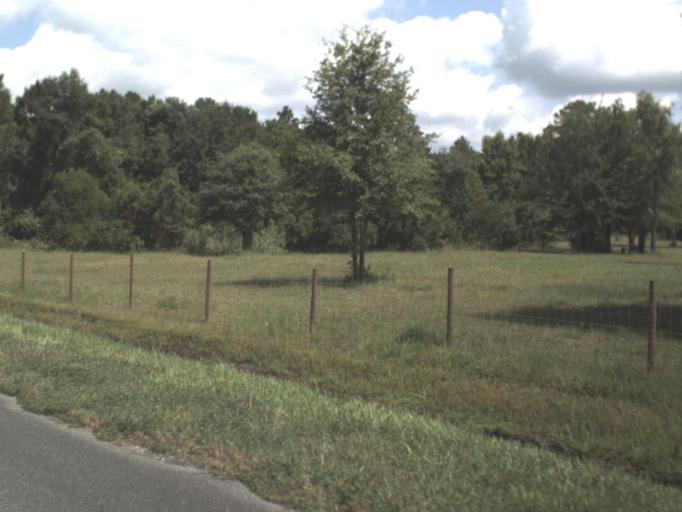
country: US
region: Florida
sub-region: Union County
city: Lake Butler
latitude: 30.0465
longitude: -82.2962
